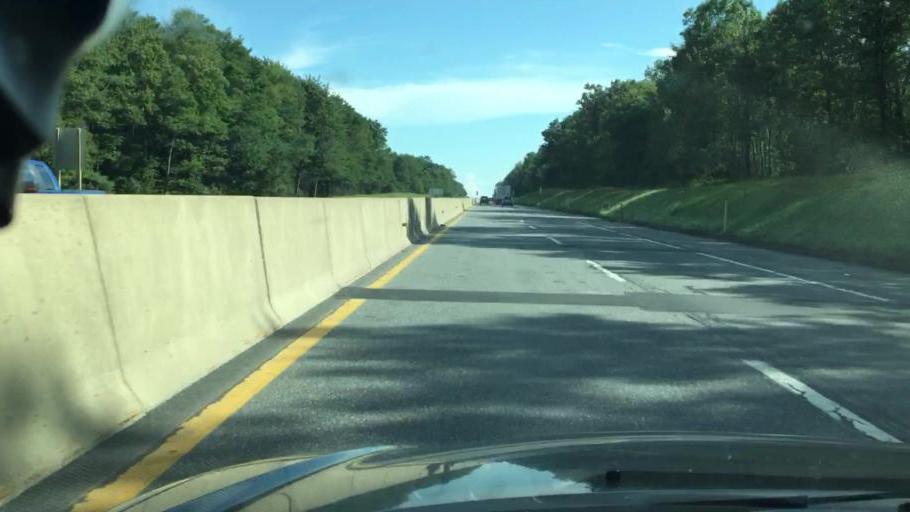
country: US
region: Pennsylvania
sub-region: Carbon County
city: Towamensing Trails
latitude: 40.9993
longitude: -75.6338
